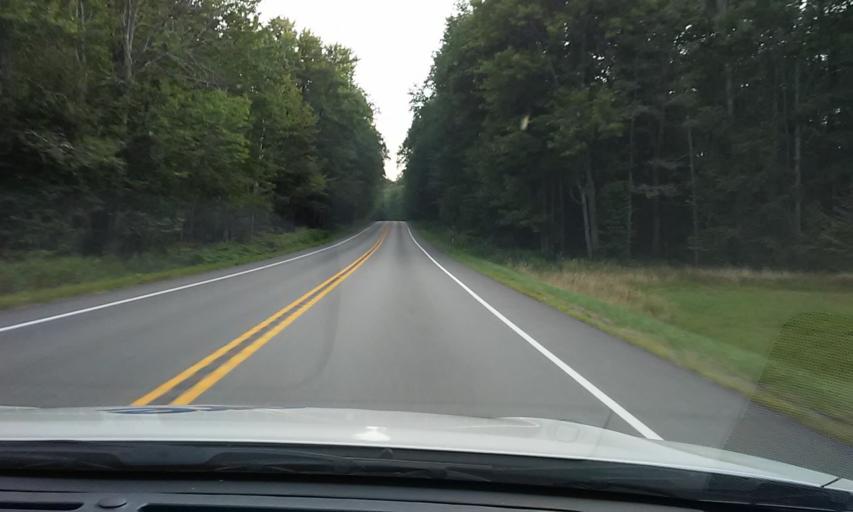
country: US
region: Pennsylvania
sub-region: Forest County
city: Marienville
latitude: 41.5161
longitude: -79.0670
